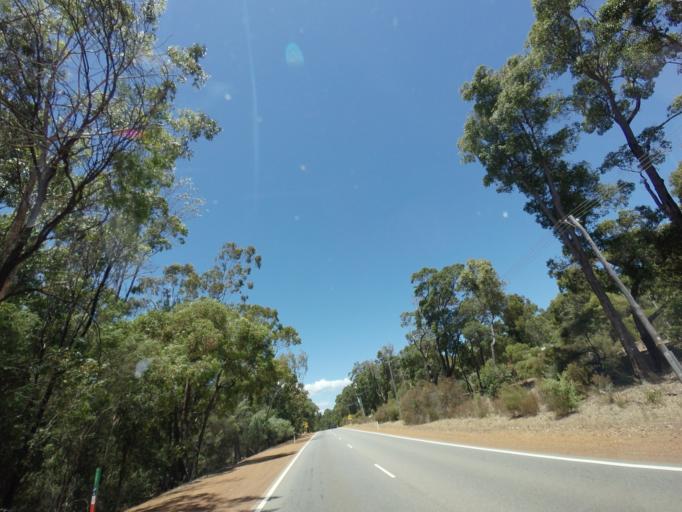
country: AU
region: Western Australia
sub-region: Mundaring
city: Parkerville
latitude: -31.8995
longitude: 116.1271
